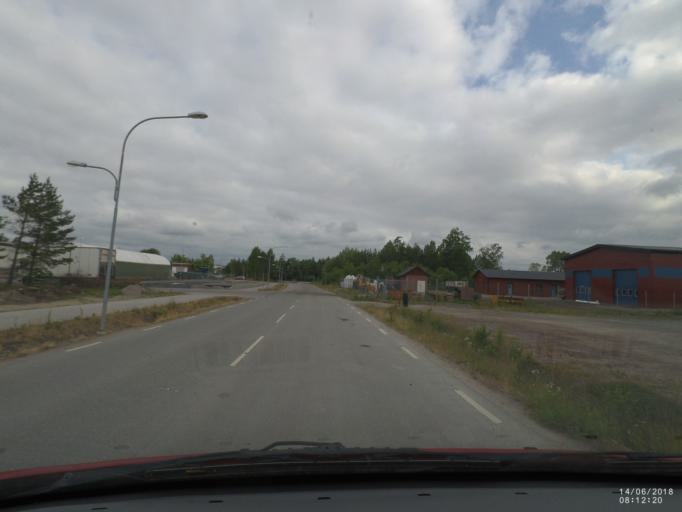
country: SE
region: Soedermanland
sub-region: Nykopings Kommun
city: Nykoping
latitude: 58.7166
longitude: 17.0329
